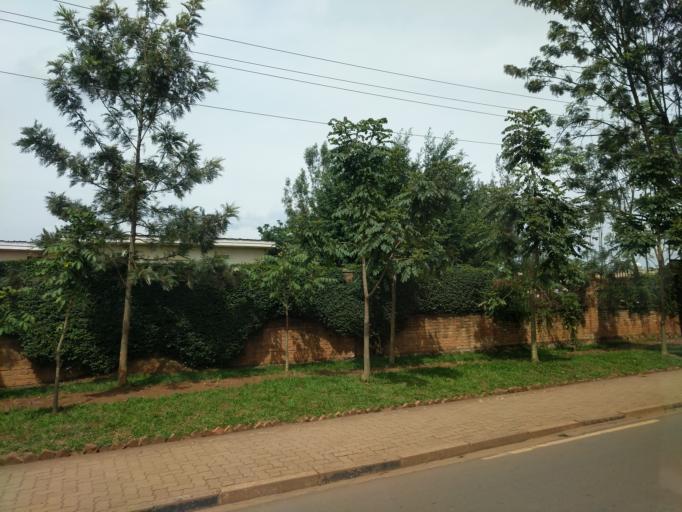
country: RW
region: Kigali
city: Kigali
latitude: -1.9764
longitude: 30.1096
